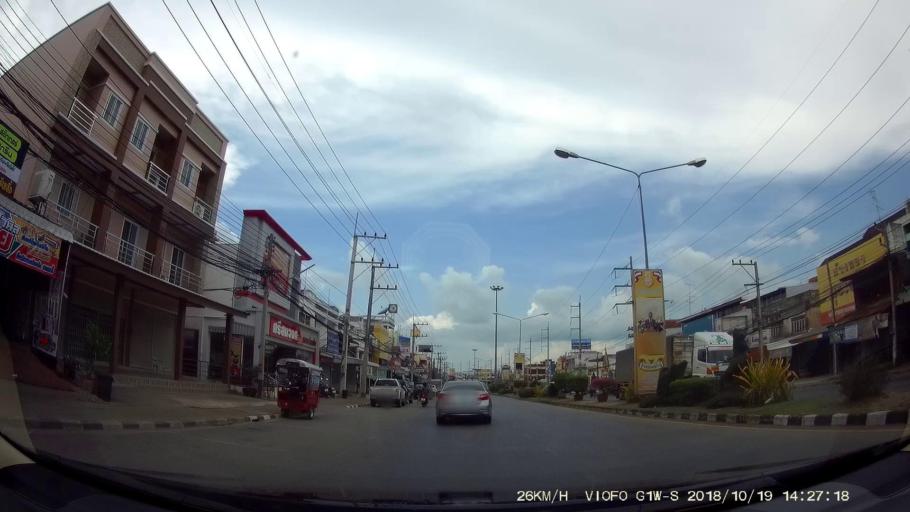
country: TH
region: Chaiyaphum
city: Kaeng Khro
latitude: 16.1109
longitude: 102.2581
